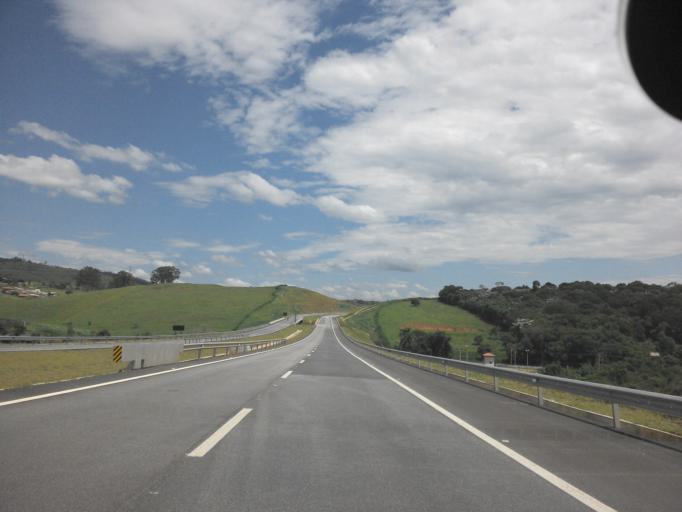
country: BR
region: Sao Paulo
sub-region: Taubate
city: Taubate
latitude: -23.0979
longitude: -45.5872
